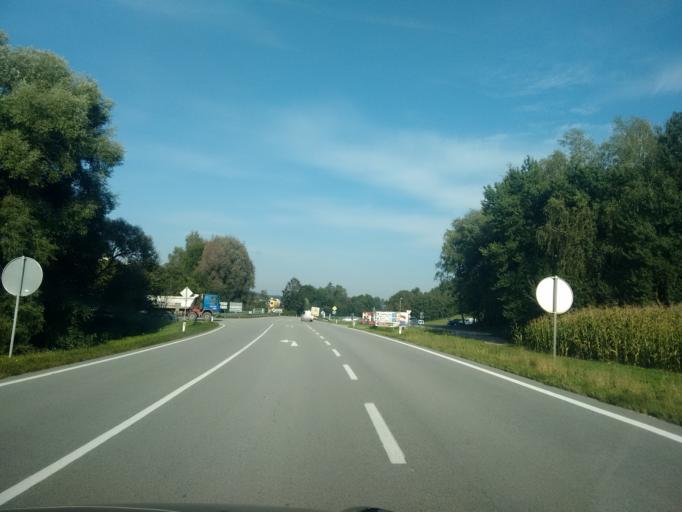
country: AT
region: Upper Austria
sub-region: Politischer Bezirk Ried im Innkreis
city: Ried im Innkreis
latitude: 48.3017
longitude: 13.6384
